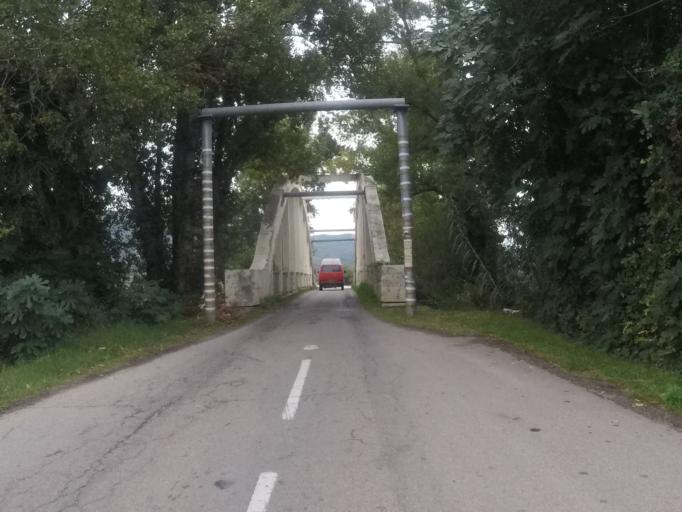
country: FR
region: Corsica
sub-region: Departement de la Corse-du-Sud
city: Propriano
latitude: 41.7266
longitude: 8.8285
